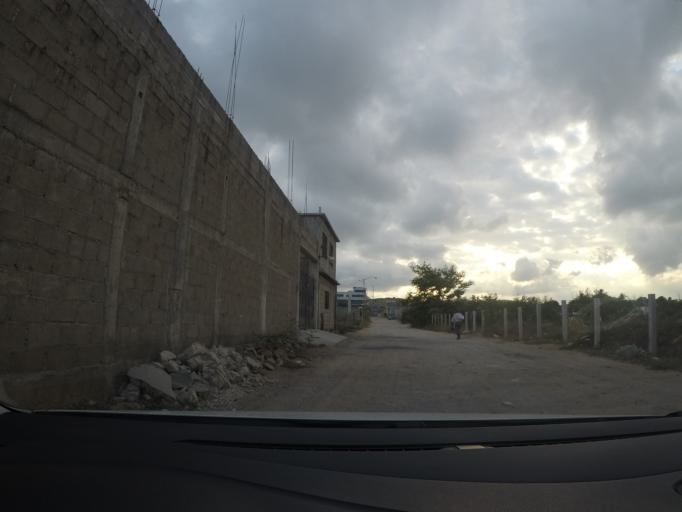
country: MX
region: Oaxaca
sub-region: Salina Cruz
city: Salina Cruz
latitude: 16.2070
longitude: -95.2015
